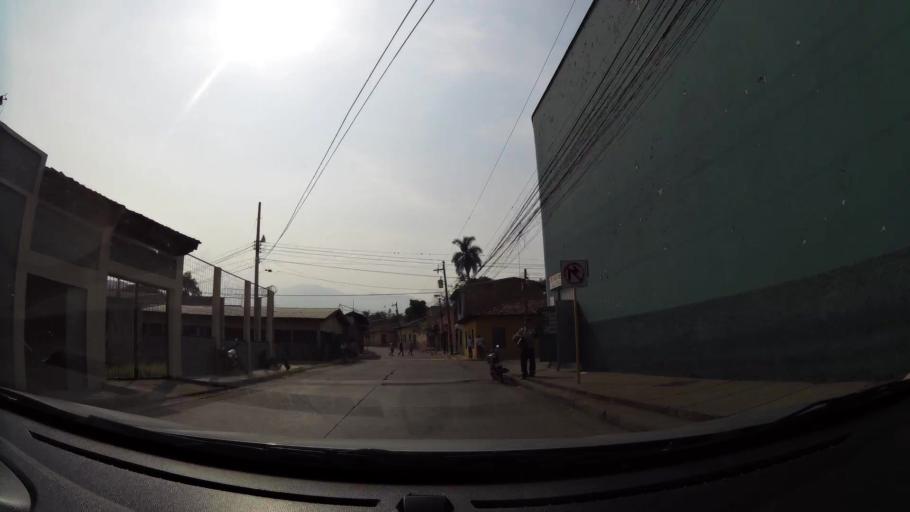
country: HN
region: Comayagua
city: Comayagua
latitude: 14.4625
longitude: -87.6431
